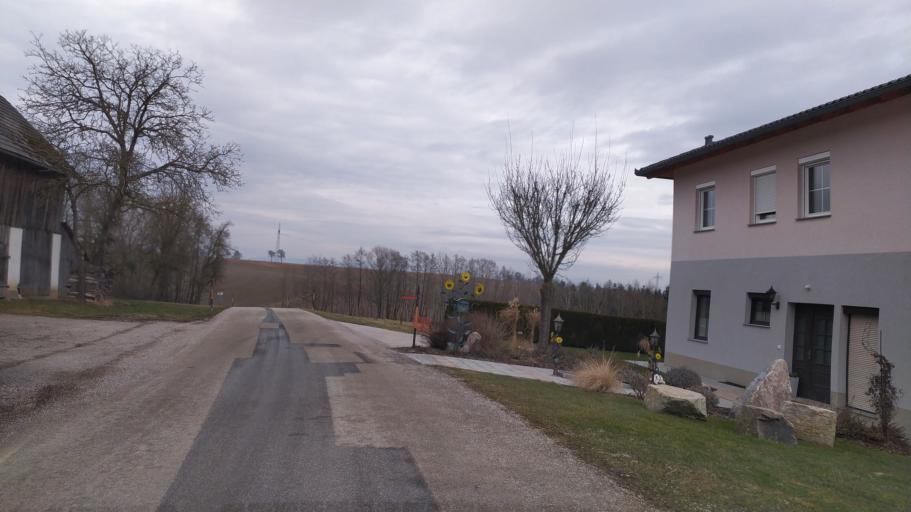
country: AT
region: Lower Austria
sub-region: Politischer Bezirk Amstetten
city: Strengberg
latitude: 48.1378
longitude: 14.7158
